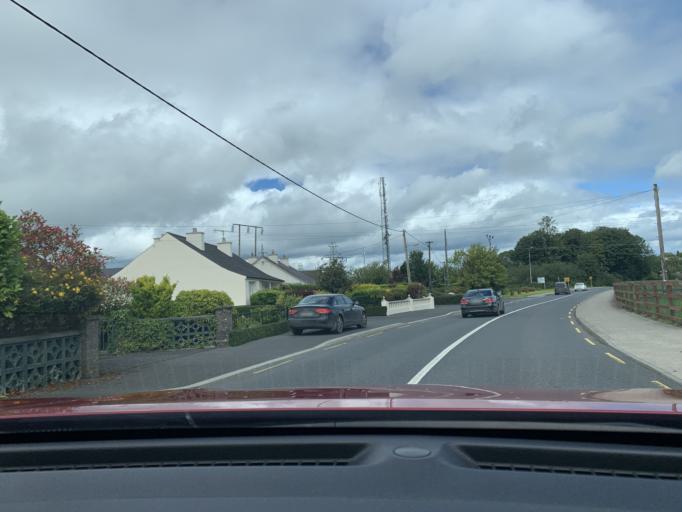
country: IE
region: Connaught
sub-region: County Leitrim
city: Carrick-on-Shannon
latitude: 53.9359
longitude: -8.1085
